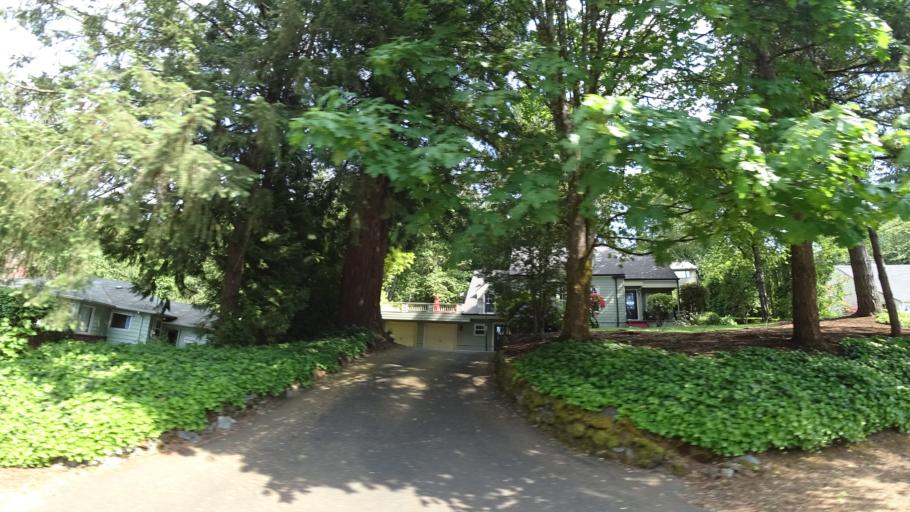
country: US
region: Oregon
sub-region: Washington County
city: Garden Home-Whitford
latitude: 45.4573
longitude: -122.7382
